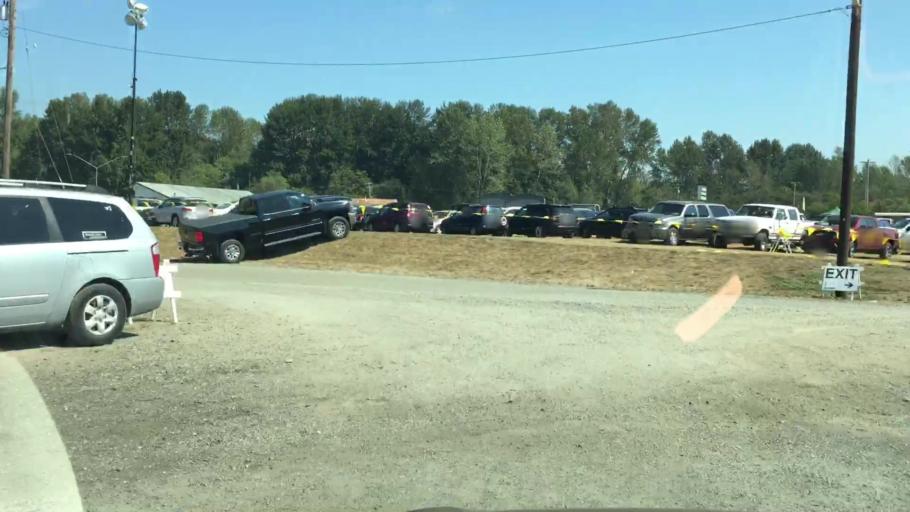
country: US
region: Washington
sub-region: Snohomish County
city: Monroe
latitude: 47.8651
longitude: -121.9849
